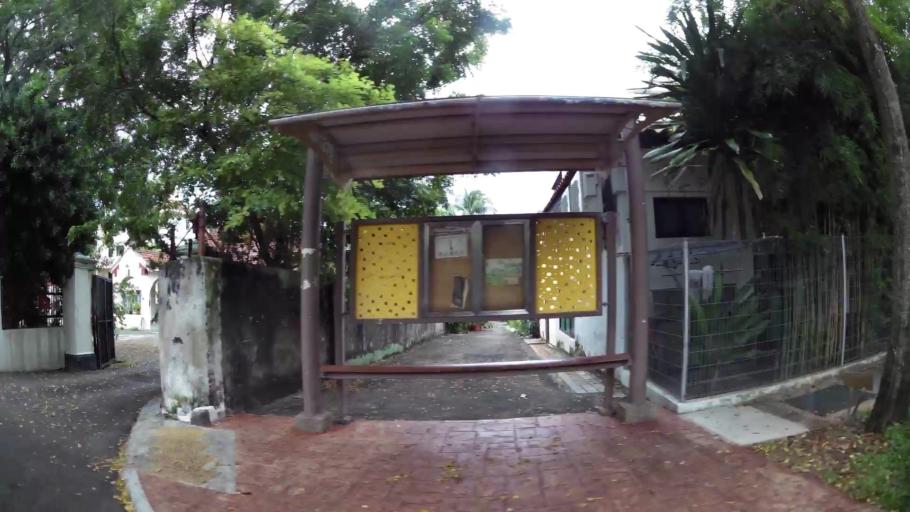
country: SG
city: Singapore
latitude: 1.3578
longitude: 103.8774
